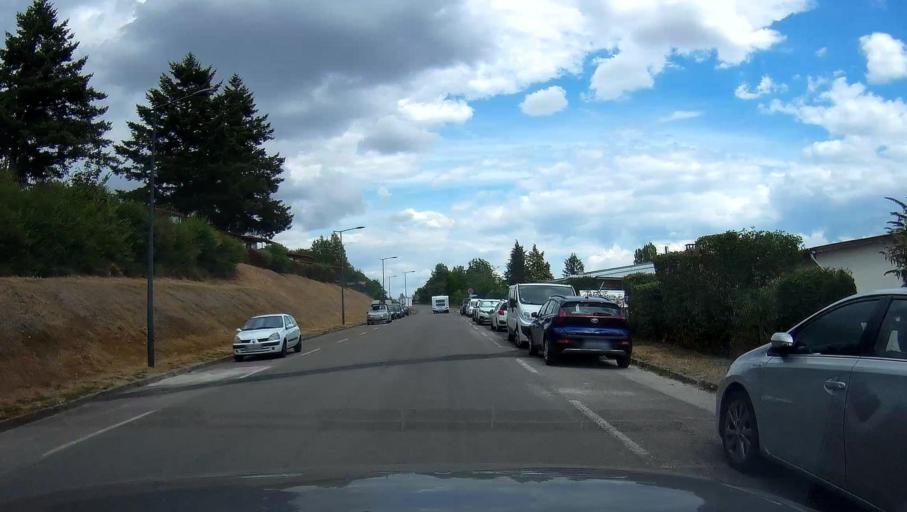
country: FR
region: Champagne-Ardenne
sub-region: Departement de la Haute-Marne
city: Langres
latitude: 47.8704
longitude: 5.3793
